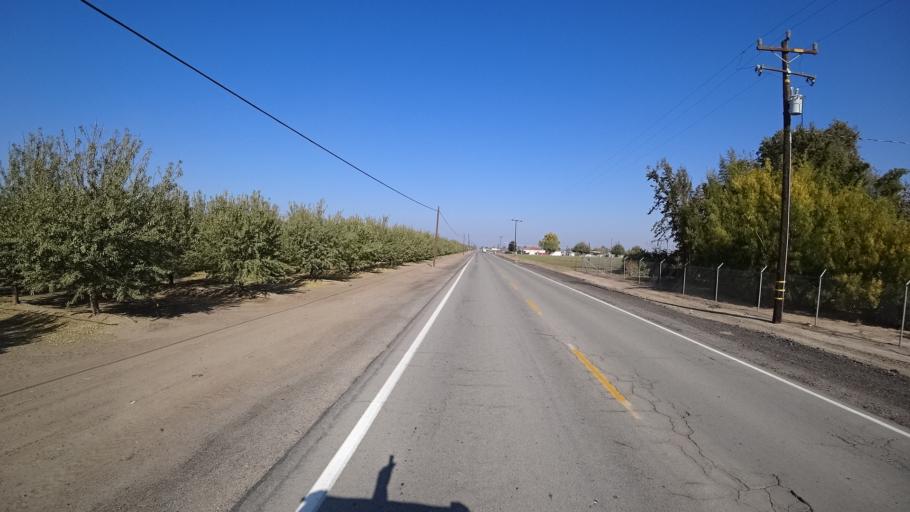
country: US
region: California
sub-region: Kern County
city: Greenfield
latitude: 35.2579
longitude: -119.0390
